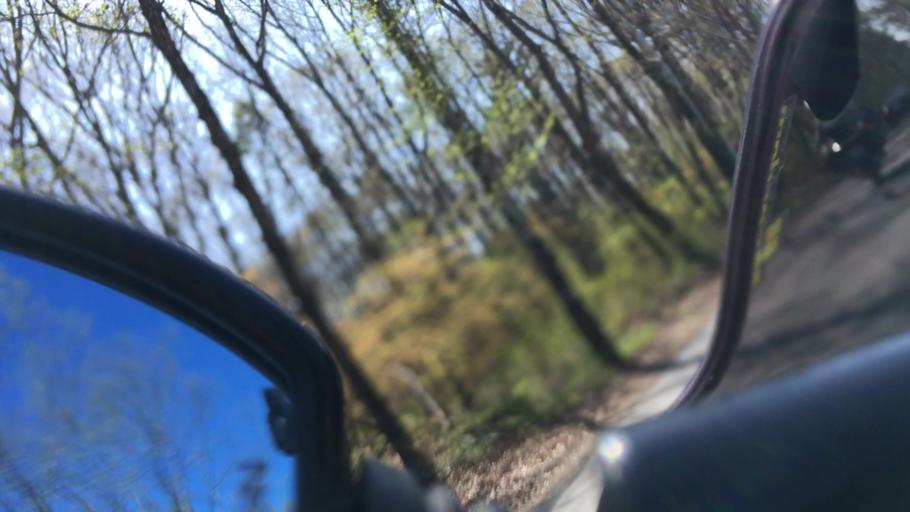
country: JP
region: Nagano
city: Komoro
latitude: 36.4631
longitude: 138.5566
